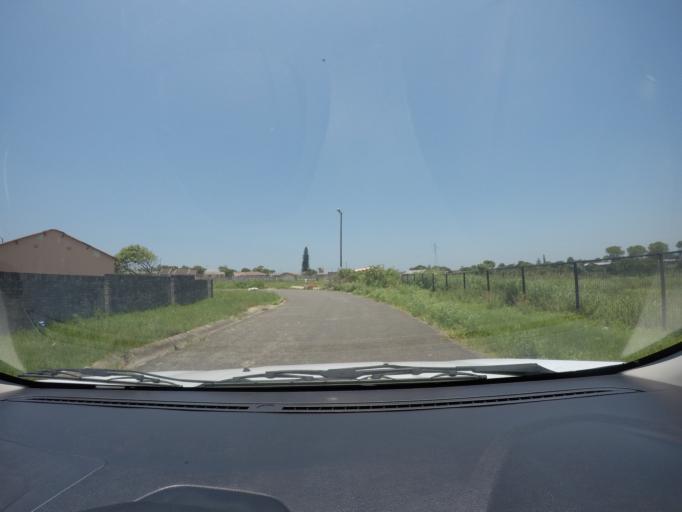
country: ZA
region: KwaZulu-Natal
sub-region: uThungulu District Municipality
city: eSikhawini
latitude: -28.8816
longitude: 31.8994
